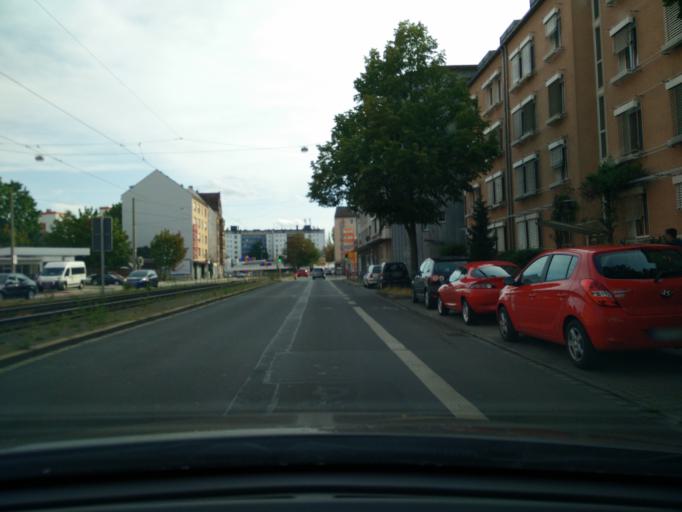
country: DE
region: Bavaria
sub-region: Regierungsbezirk Mittelfranken
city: Nuernberg
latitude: 49.4303
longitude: 11.0661
